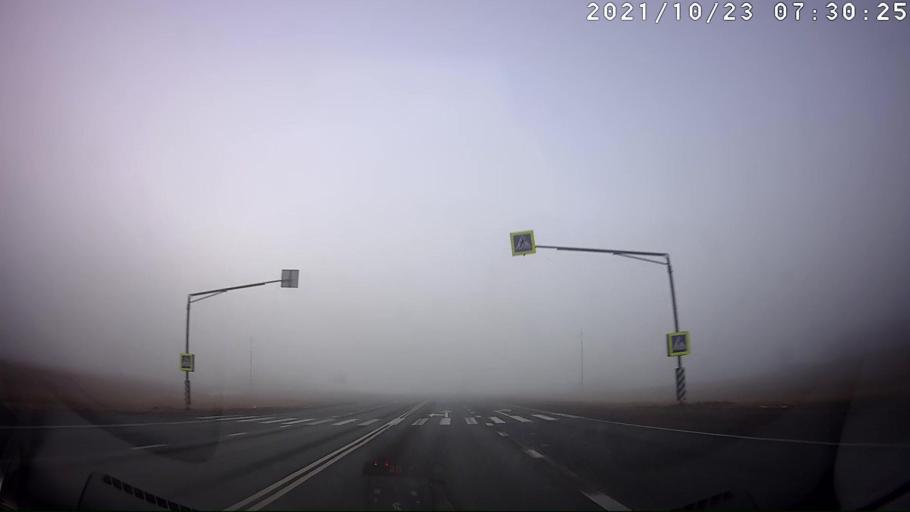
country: RU
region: Saratov
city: Alekseyevka
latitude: 52.2954
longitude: 47.9287
